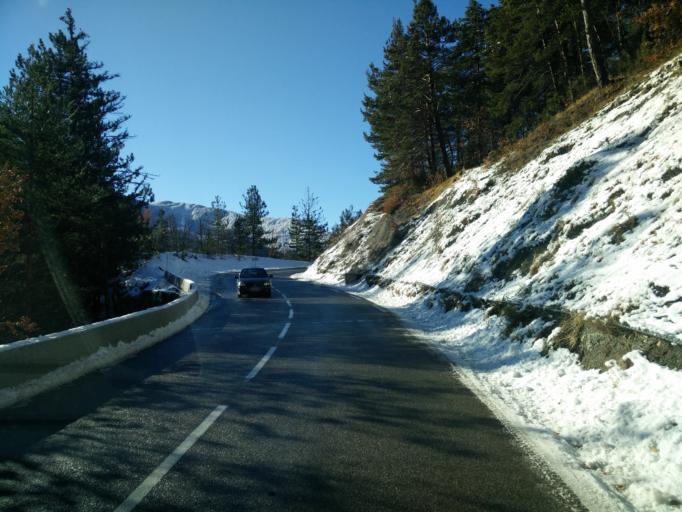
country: FR
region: Provence-Alpes-Cote d'Azur
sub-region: Departement des Alpes-de-Haute-Provence
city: Annot
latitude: 43.9344
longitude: 6.6348
